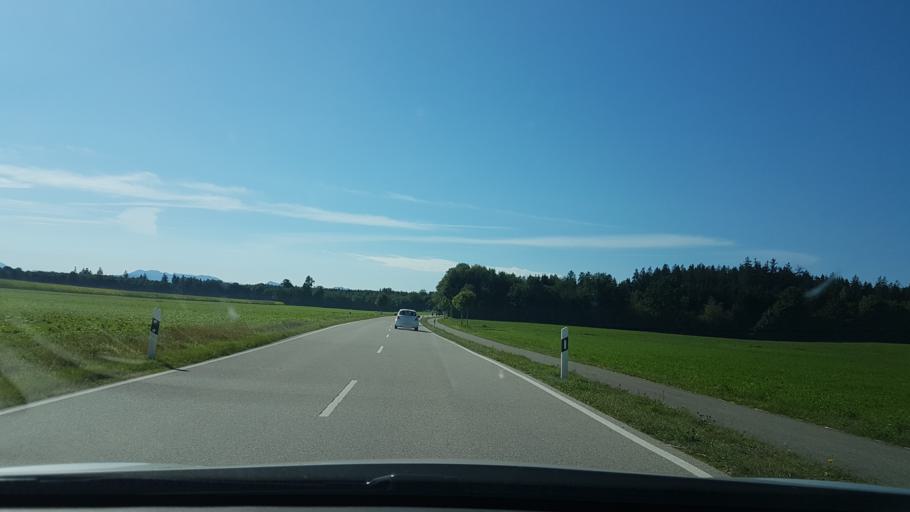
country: DE
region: Bavaria
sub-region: Upper Bavaria
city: Valley
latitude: 47.9059
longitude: 11.7667
